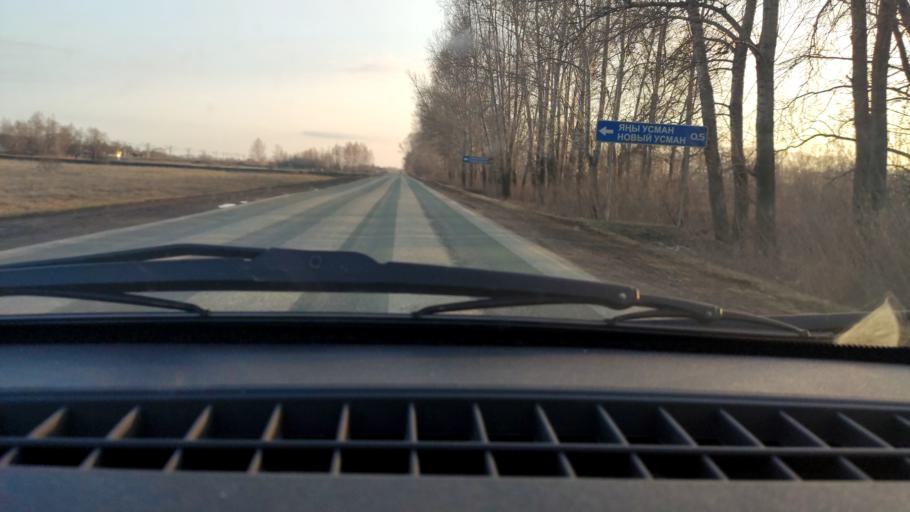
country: RU
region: Bashkortostan
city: Chishmy
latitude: 54.4529
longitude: 55.2496
